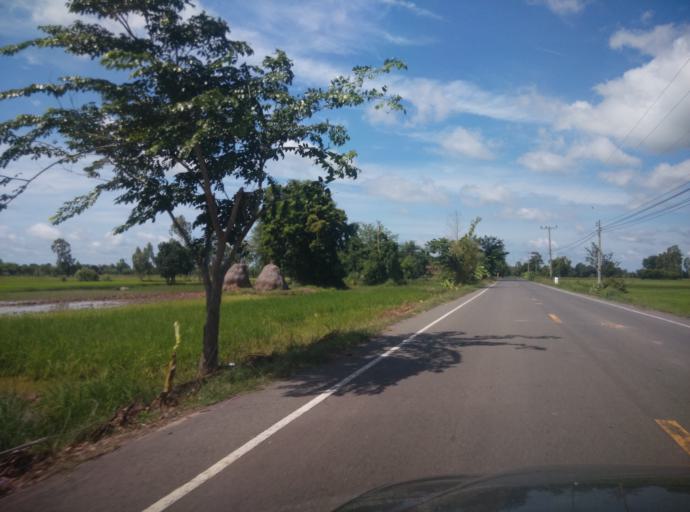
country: TH
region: Sisaket
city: Huai Thap Than
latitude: 14.9807
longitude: 104.0697
